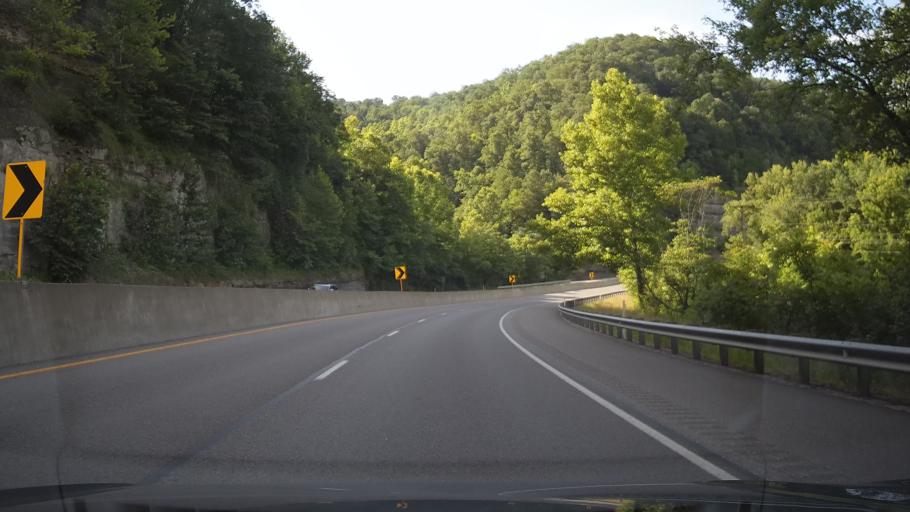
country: US
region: Kentucky
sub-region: Lawrence County
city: Louisa
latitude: 37.9773
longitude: -82.6718
